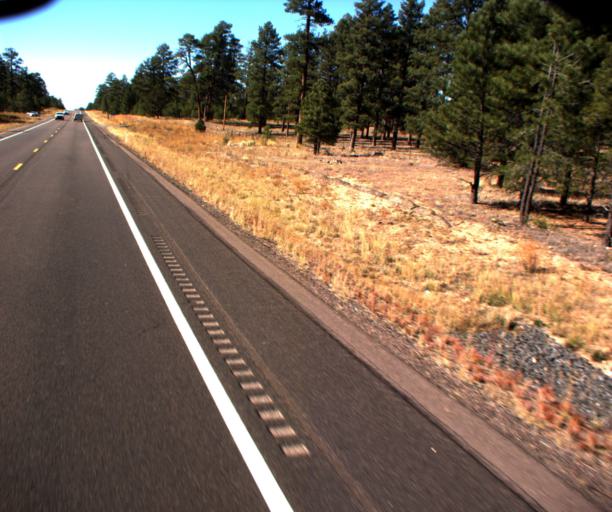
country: US
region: Arizona
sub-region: Apache County
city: Saint Michaels
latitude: 35.6923
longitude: -109.2617
